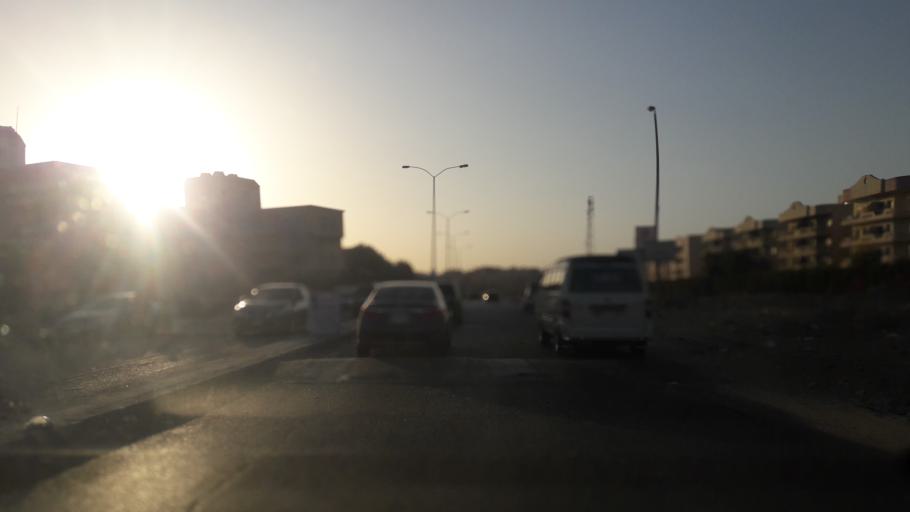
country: EG
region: Al Jizah
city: Madinat Sittah Uktubar
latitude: 29.9478
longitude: 30.9430
